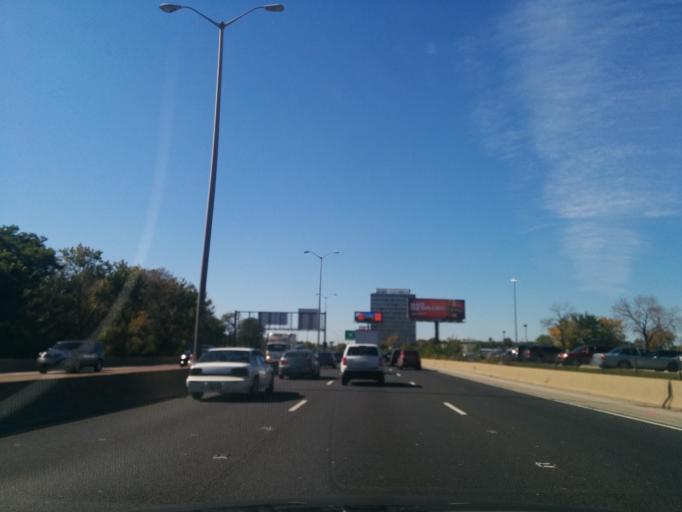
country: US
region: Illinois
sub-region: Cook County
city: Forest Park
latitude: 41.8721
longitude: -87.8263
